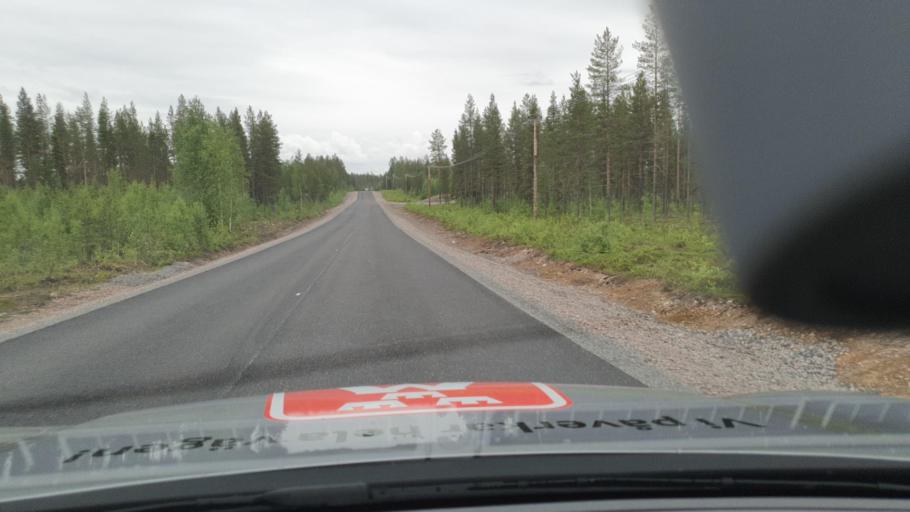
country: SE
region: Norrbotten
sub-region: Overtornea Kommun
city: OEvertornea
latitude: 66.6492
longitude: 23.2373
